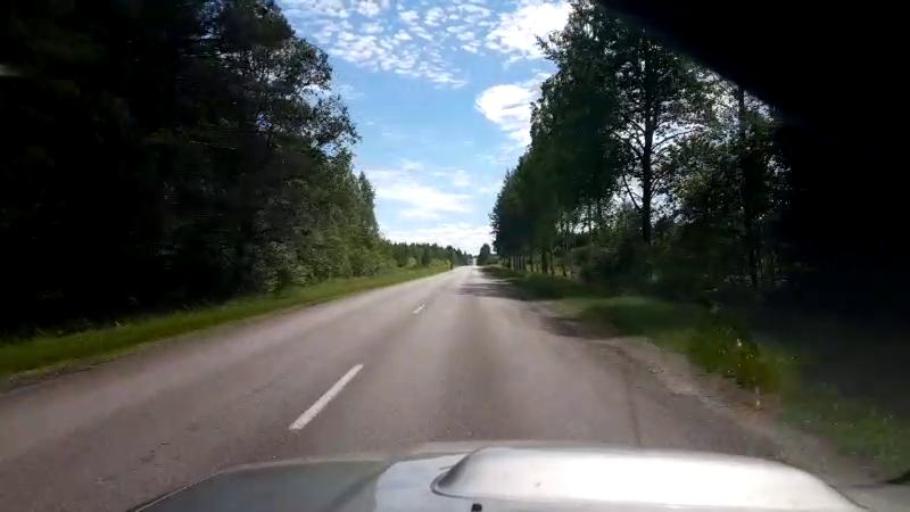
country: EE
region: Laeaene-Virumaa
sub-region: Rakke vald
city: Rakke
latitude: 58.8736
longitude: 26.2957
